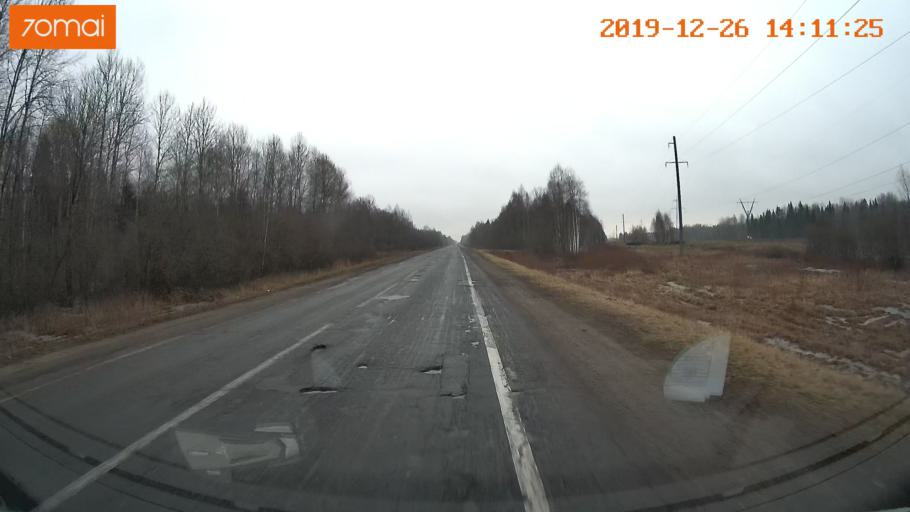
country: RU
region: Jaroslavl
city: Poshekhon'ye
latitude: 58.5095
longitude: 38.9721
